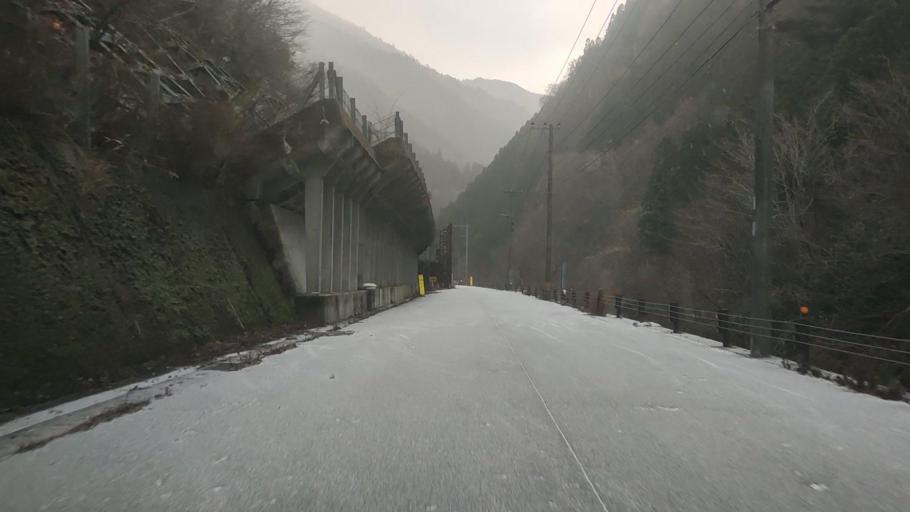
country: JP
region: Kumamoto
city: Matsubase
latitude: 32.5543
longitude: 130.9292
